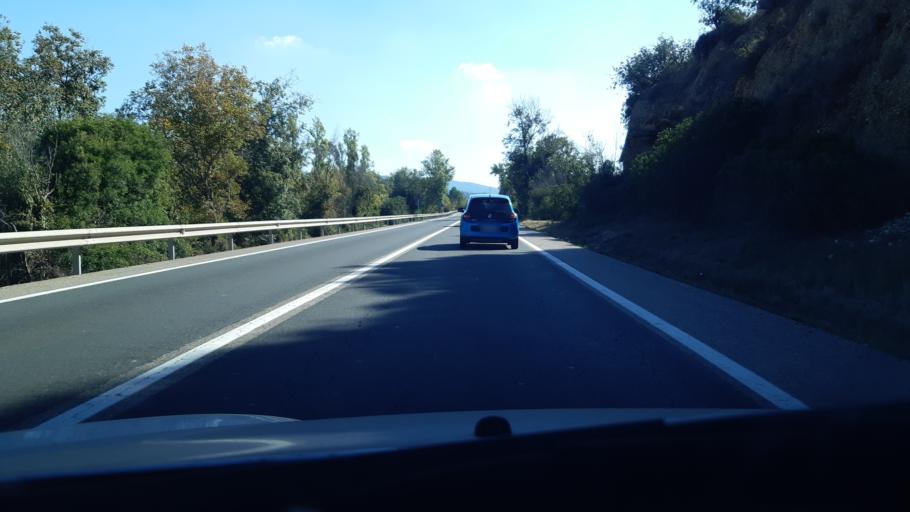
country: ES
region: Catalonia
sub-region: Provincia de Tarragona
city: Tivenys
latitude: 40.8599
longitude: 0.5098
